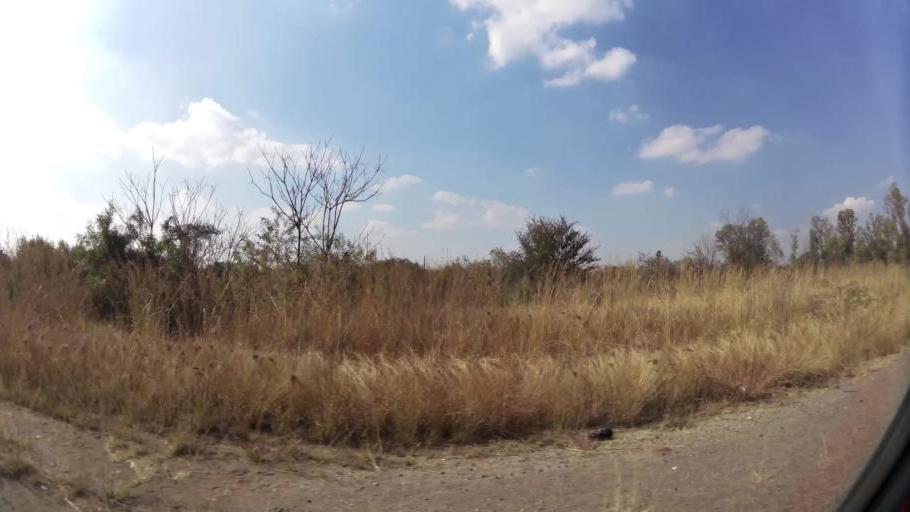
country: ZA
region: North-West
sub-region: Bojanala Platinum District Municipality
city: Rustenburg
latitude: -25.5170
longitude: 27.1015
